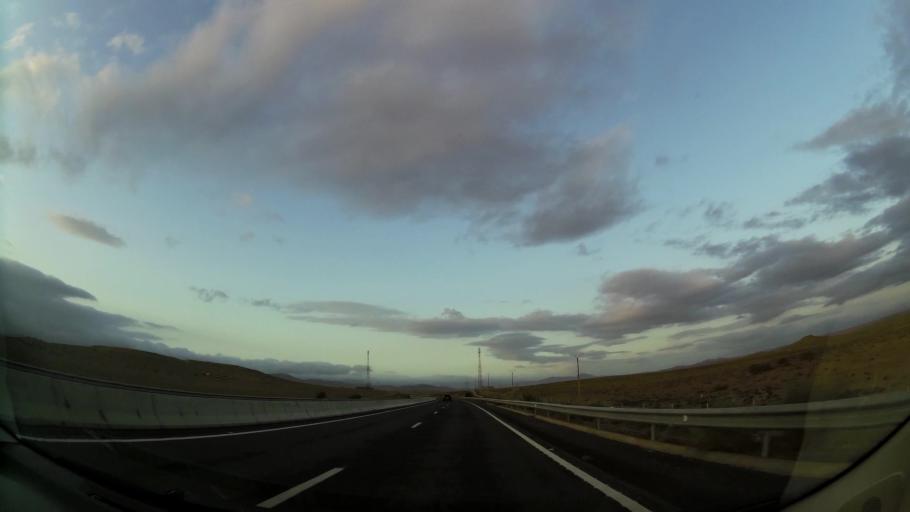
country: MA
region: Oriental
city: Taourirt
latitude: 34.5556
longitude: -2.8448
